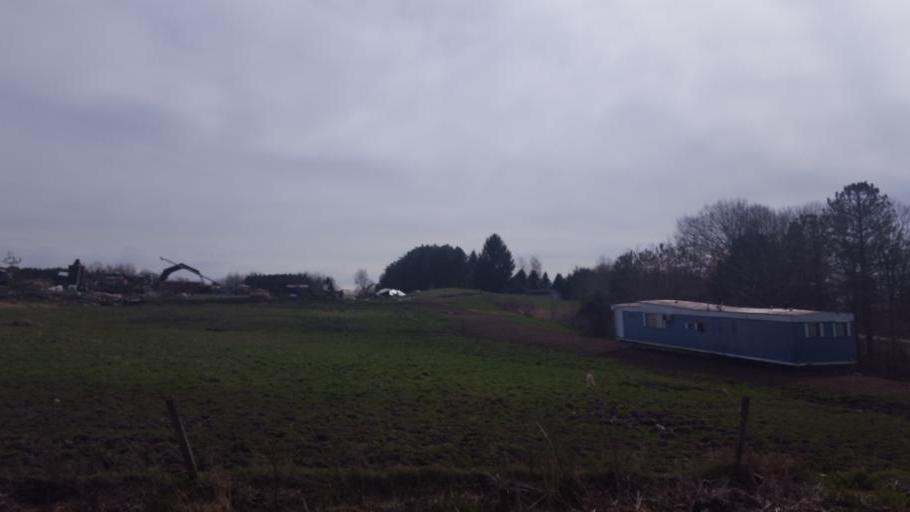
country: US
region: Michigan
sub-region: Gladwin County
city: Gladwin
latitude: 43.9879
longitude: -84.5348
